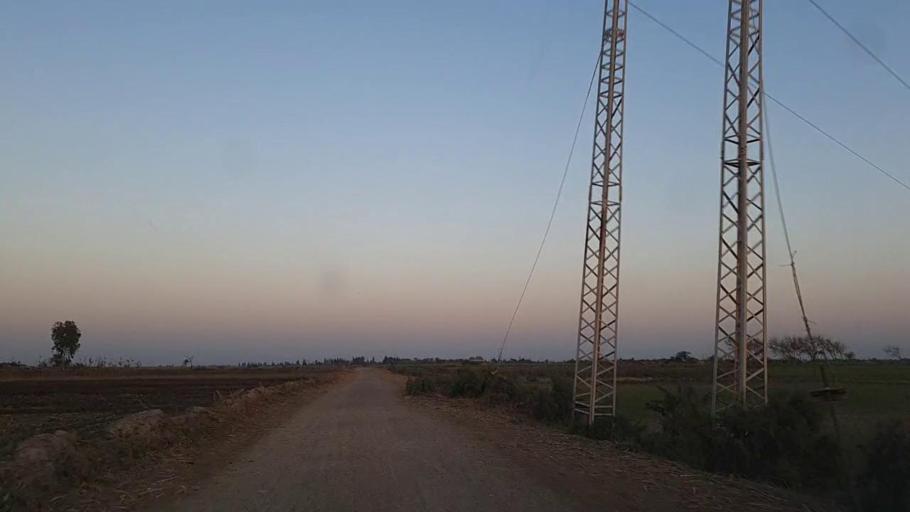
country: PK
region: Sindh
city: Samaro
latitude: 25.3106
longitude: 69.4033
